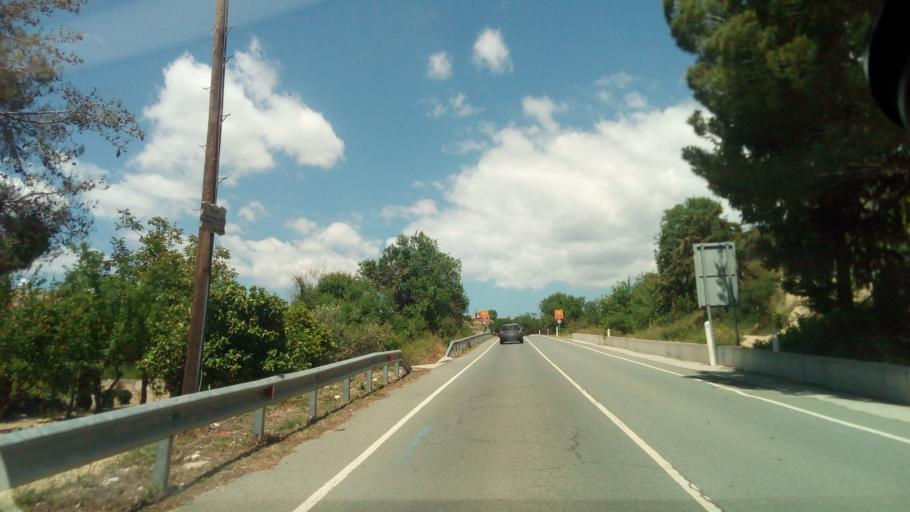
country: CY
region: Limassol
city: Pachna
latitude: 34.7826
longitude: 32.8280
